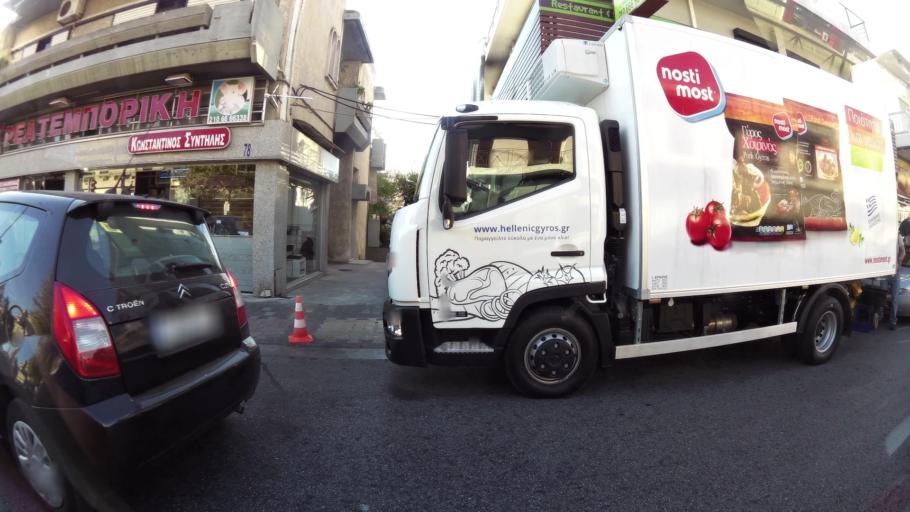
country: GR
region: Attica
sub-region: Nomarchia Anatolikis Attikis
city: Pallini
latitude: 38.0037
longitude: 23.8805
